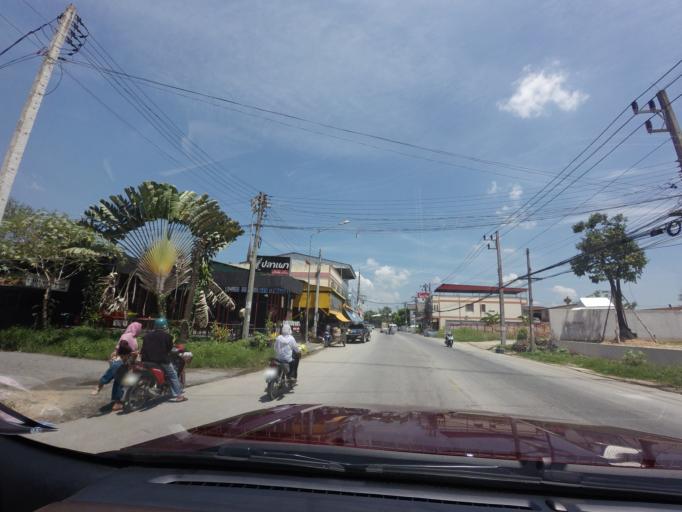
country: TH
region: Yala
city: Yala
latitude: 6.5548
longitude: 101.2716
